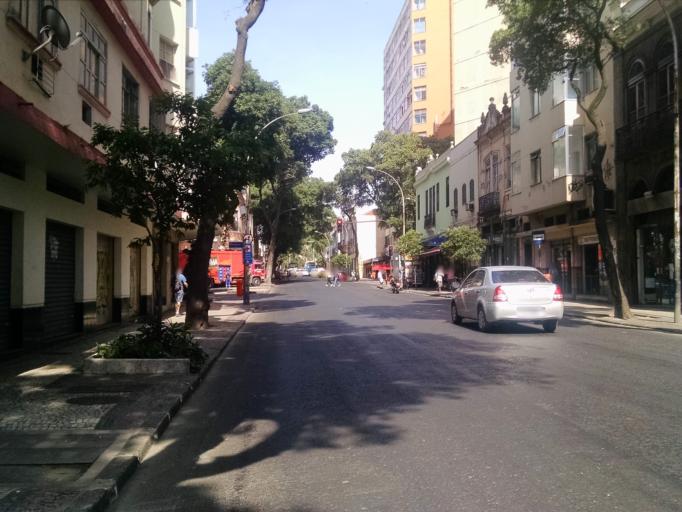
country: BR
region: Rio de Janeiro
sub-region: Rio De Janeiro
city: Rio de Janeiro
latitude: -22.9126
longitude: -43.1849
